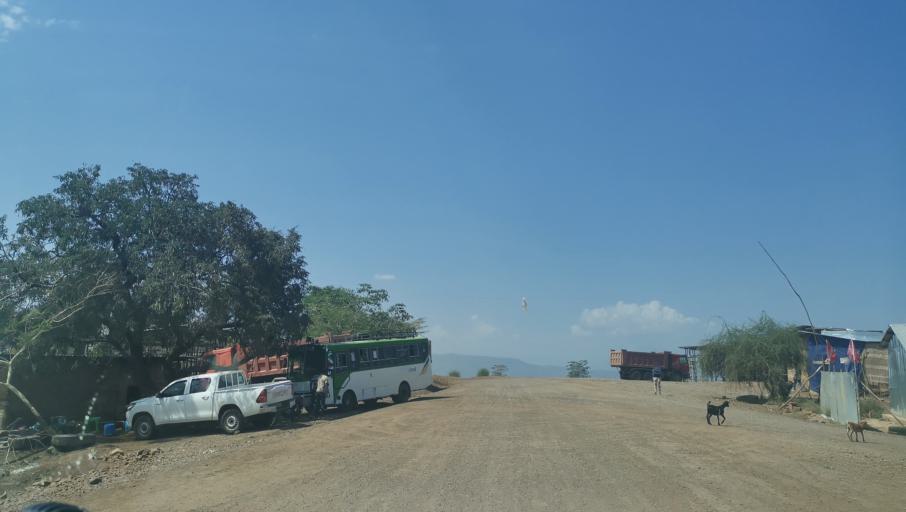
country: ET
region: Southern Nations, Nationalities, and People's Region
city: Arba Minch'
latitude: 6.3402
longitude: 37.3161
